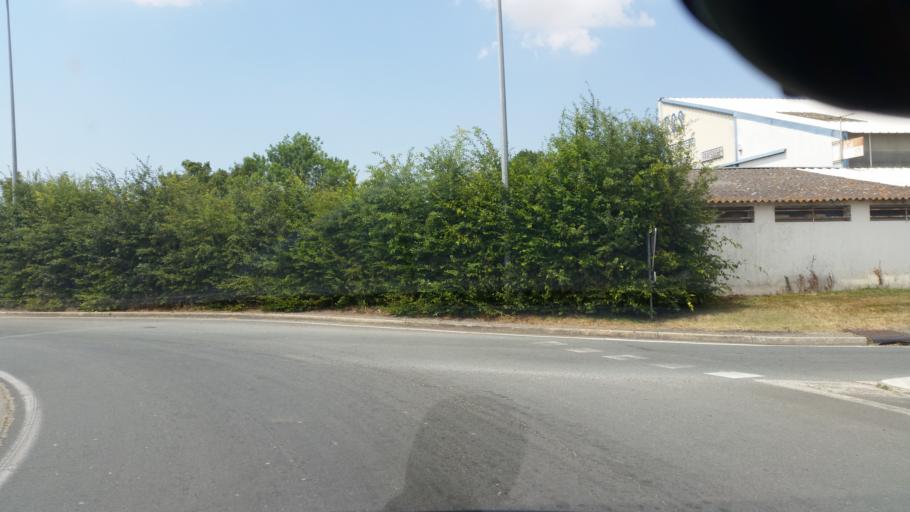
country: FR
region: Poitou-Charentes
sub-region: Departement de la Charente-Maritime
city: Surgeres
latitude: 46.1088
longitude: -0.7693
